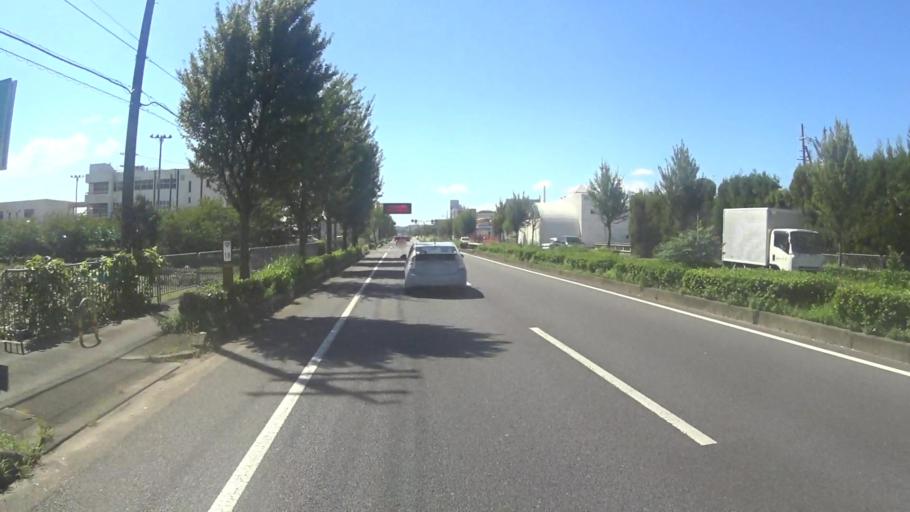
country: JP
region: Kyoto
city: Tanabe
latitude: 34.8643
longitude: 135.7625
